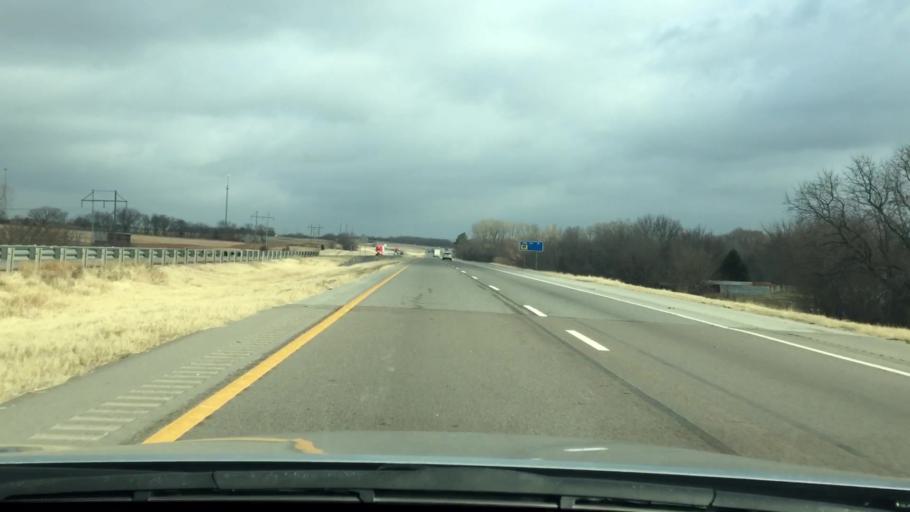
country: US
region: Oklahoma
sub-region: McClain County
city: Purcell
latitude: 35.0303
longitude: -97.3758
